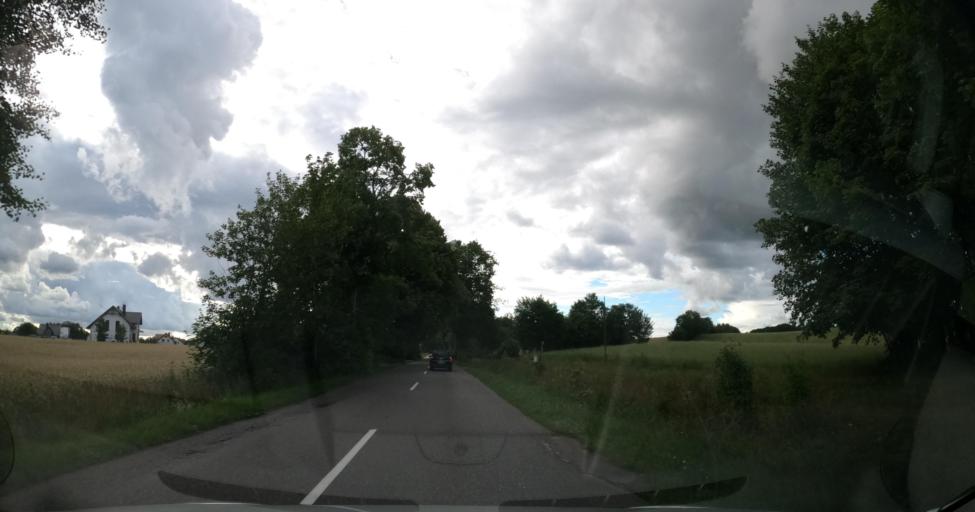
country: PL
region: Pomeranian Voivodeship
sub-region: Powiat kartuski
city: Suleczyno
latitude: 54.3338
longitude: 17.7692
